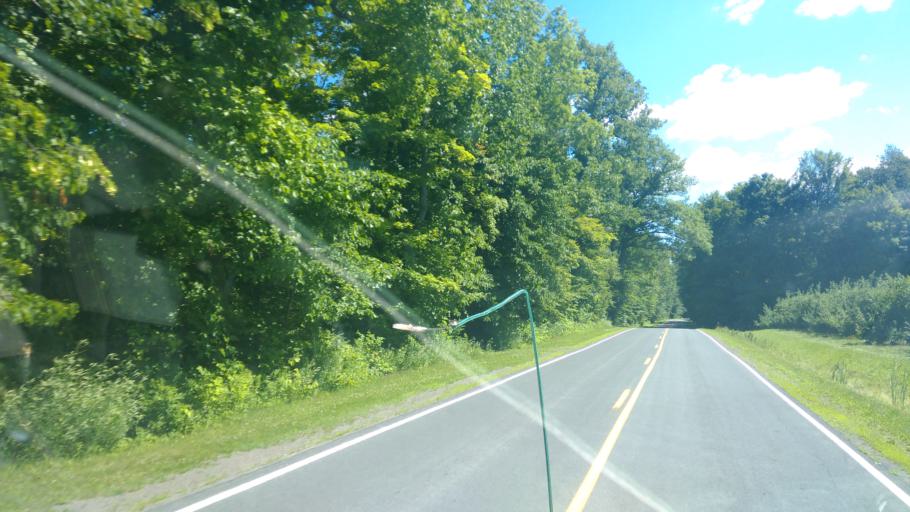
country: US
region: New York
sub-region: Wayne County
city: Sodus
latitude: 43.1957
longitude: -77.0493
